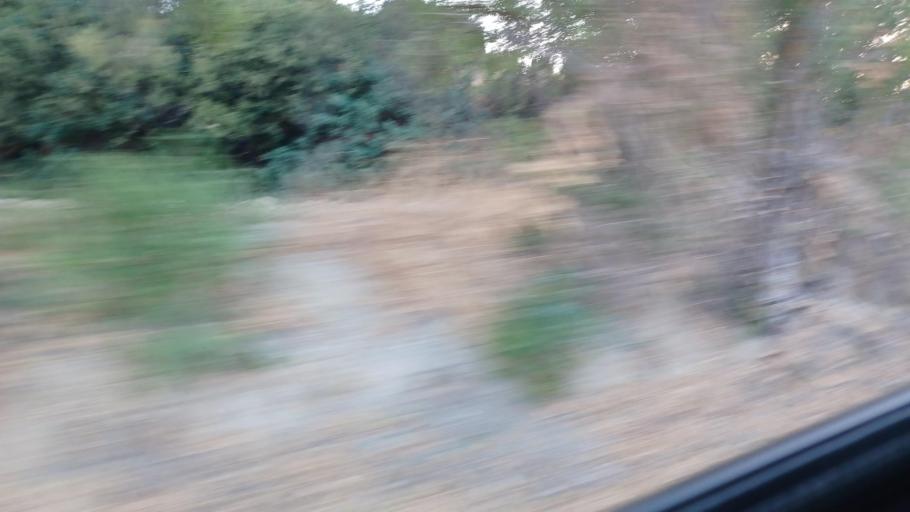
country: CY
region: Pafos
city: Mesogi
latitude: 34.8305
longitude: 32.5667
